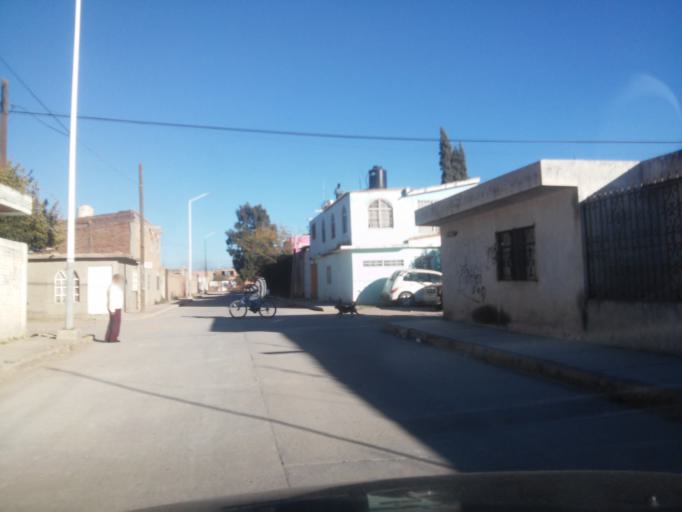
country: MX
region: Durango
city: Victoria de Durango
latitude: 24.0146
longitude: -104.6347
